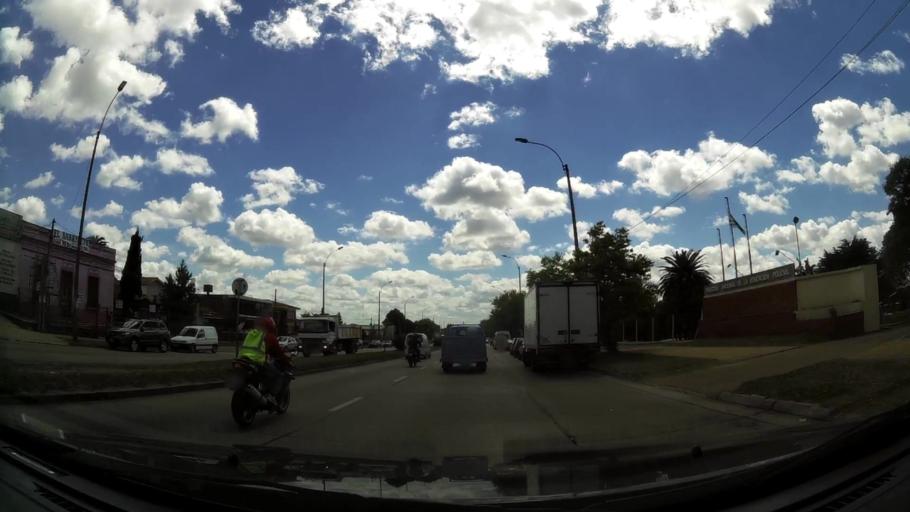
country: UY
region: Canelones
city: Paso de Carrasco
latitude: -34.8377
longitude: -56.1176
